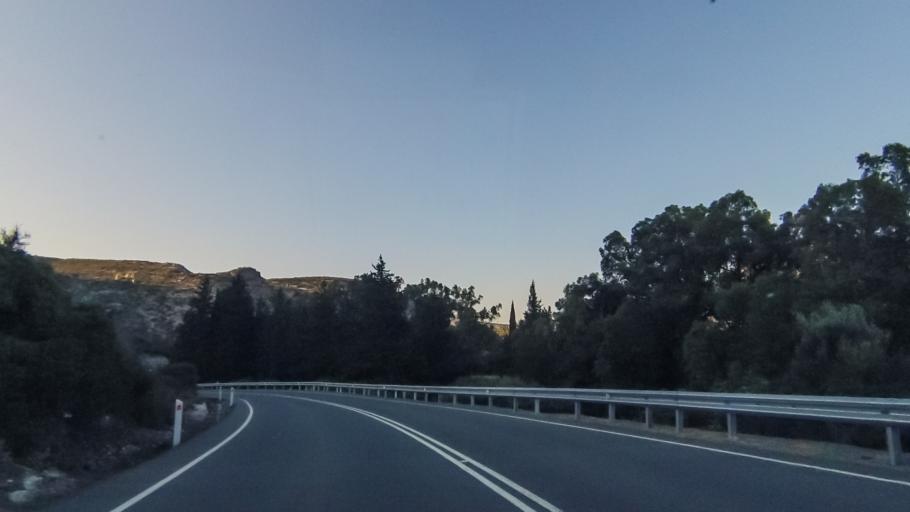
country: CY
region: Limassol
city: Sotira
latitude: 34.6748
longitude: 32.8207
